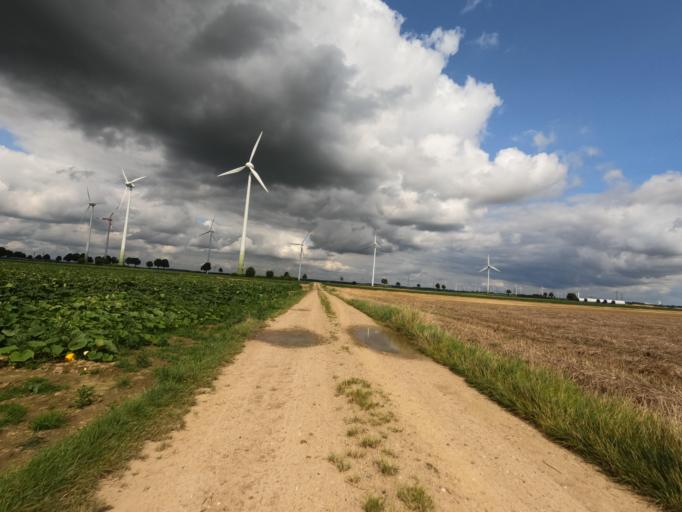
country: DE
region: North Rhine-Westphalia
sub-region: Regierungsbezirk Koln
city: Linnich
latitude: 50.9841
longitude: 6.2278
